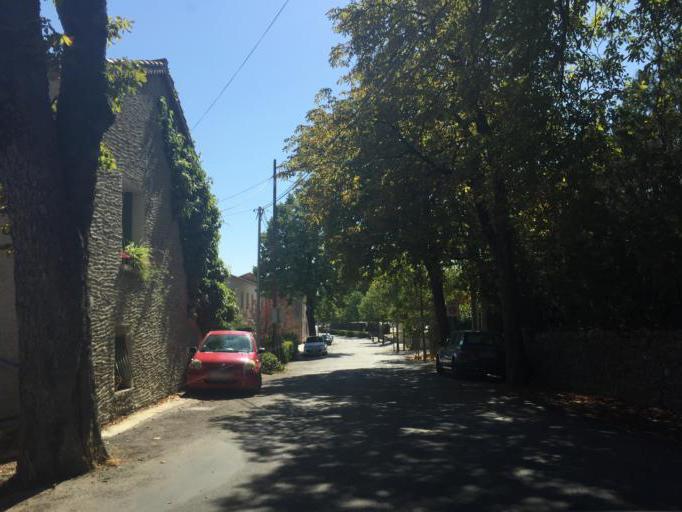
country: FR
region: Provence-Alpes-Cote d'Azur
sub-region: Departement des Alpes-de-Haute-Provence
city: Forcalquier
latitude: 43.9623
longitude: 5.7826
